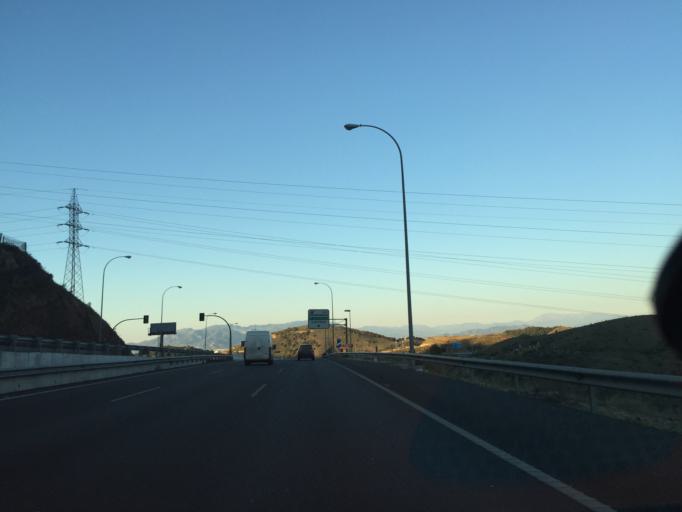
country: ES
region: Andalusia
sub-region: Provincia de Malaga
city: Malaga
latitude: 36.7399
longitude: -4.3877
